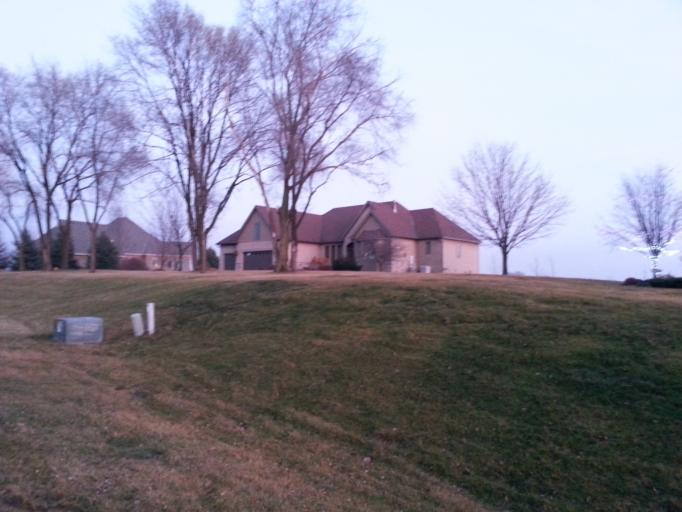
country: US
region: Minnesota
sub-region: Washington County
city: Lakeland
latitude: 44.9541
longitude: -92.8302
